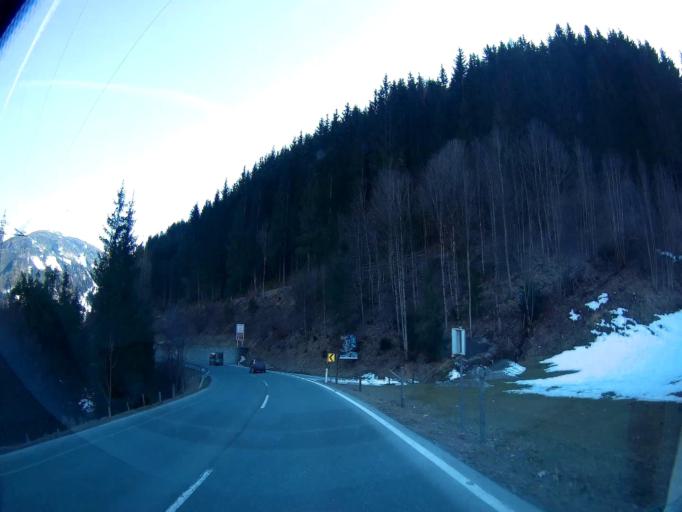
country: AT
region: Salzburg
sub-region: Politischer Bezirk Sankt Johann im Pongau
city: Bad Gastein
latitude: 47.1398
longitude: 13.1231
